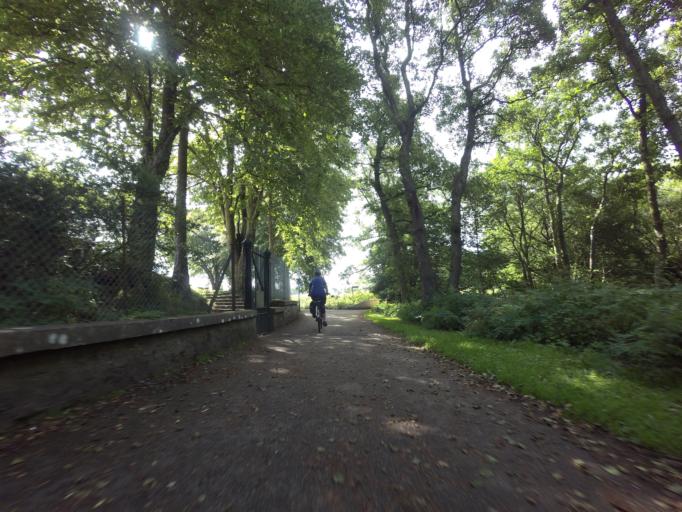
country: GB
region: Scotland
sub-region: Highland
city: Nairn
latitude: 57.5810
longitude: -3.8631
